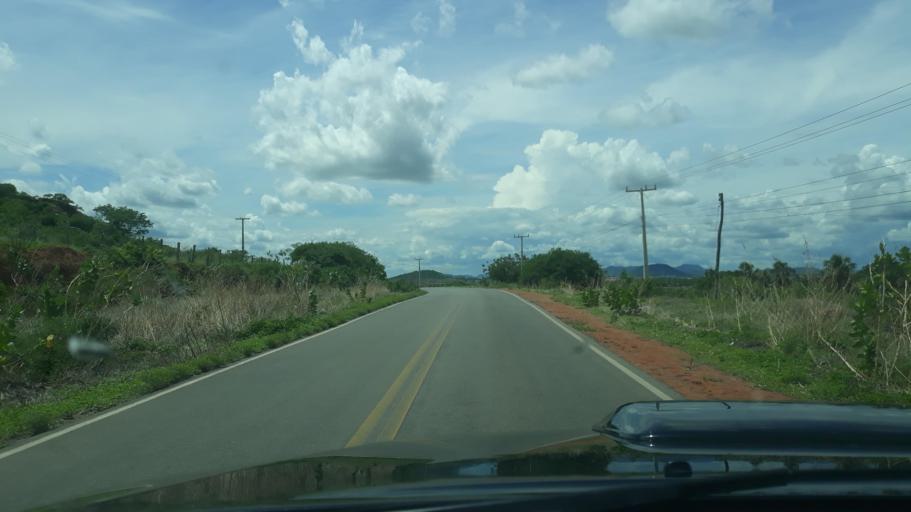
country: BR
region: Bahia
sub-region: Guanambi
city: Guanambi
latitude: -14.2611
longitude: -42.7231
